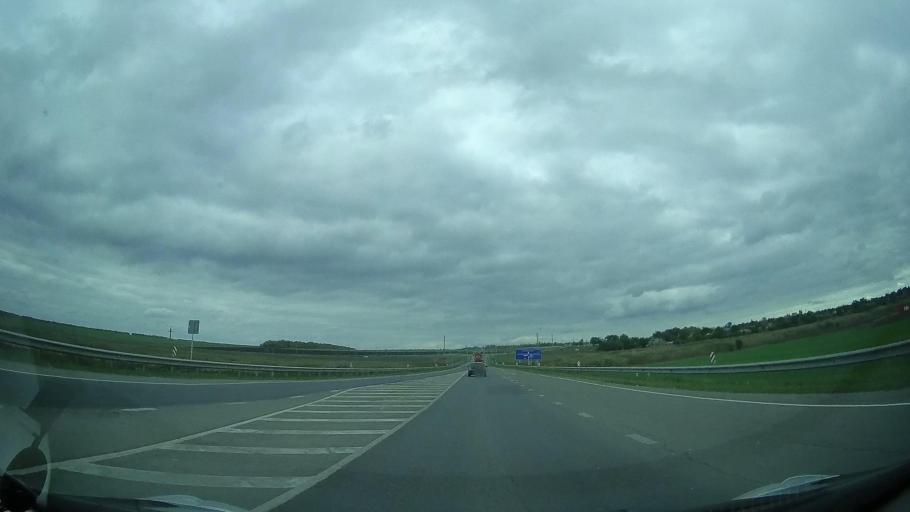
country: RU
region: Rostov
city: Yegorlykskaya
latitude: 46.5619
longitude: 40.6286
